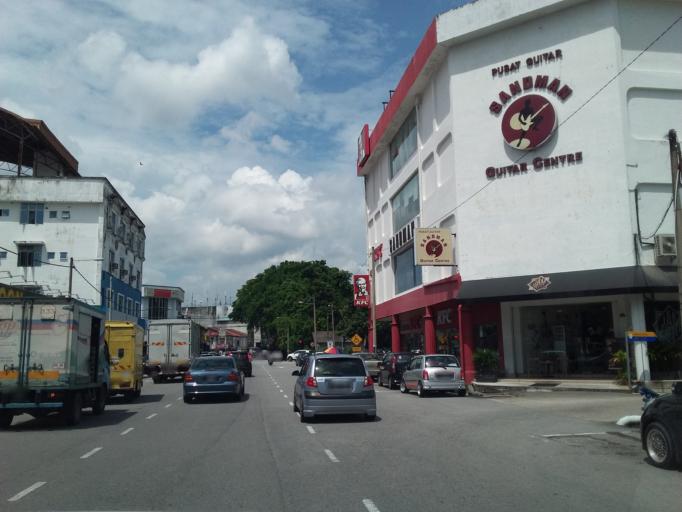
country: MY
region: Johor
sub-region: Daerah Batu Pahat
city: Batu Pahat
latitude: 1.8524
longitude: 102.9261
